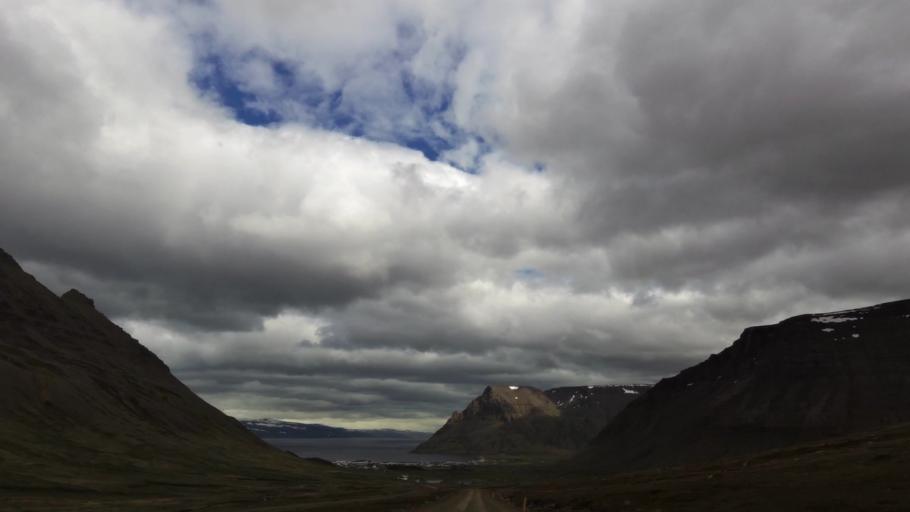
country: IS
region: Westfjords
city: Isafjoerdur
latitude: 66.1626
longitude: -23.3151
